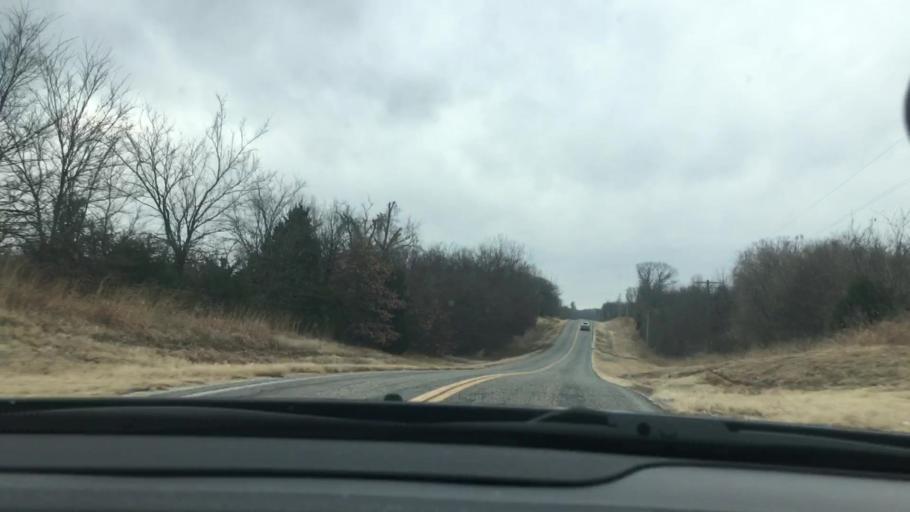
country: US
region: Oklahoma
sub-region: Johnston County
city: Tishomingo
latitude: 34.2226
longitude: -96.6361
